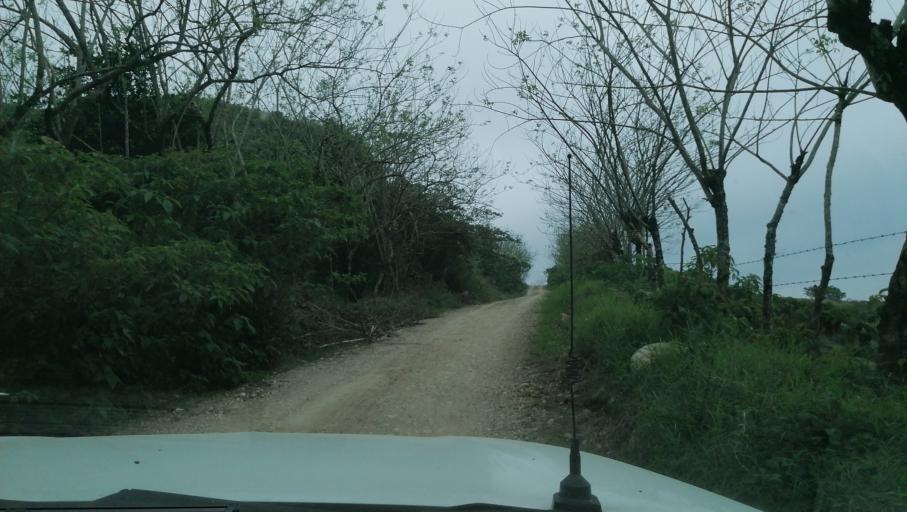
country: MX
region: Chiapas
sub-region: Francisco Leon
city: San Miguel la Sardina
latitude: 17.2909
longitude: -93.2846
